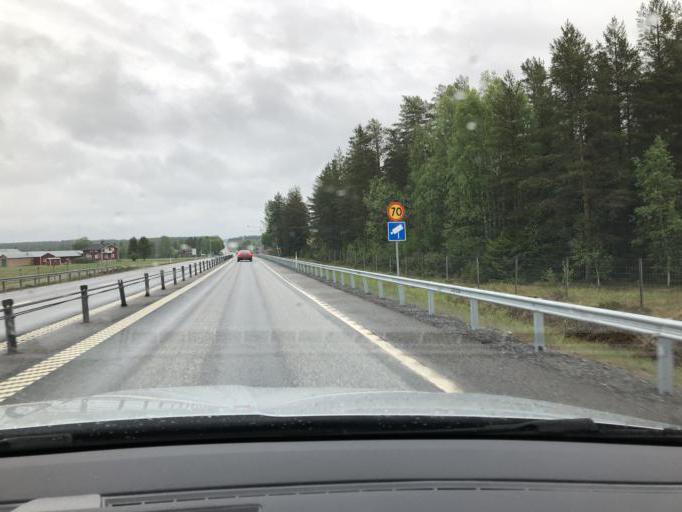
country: SE
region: Vaesterbotten
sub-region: Umea Kommun
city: Hoernefors
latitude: 63.6778
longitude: 19.9929
